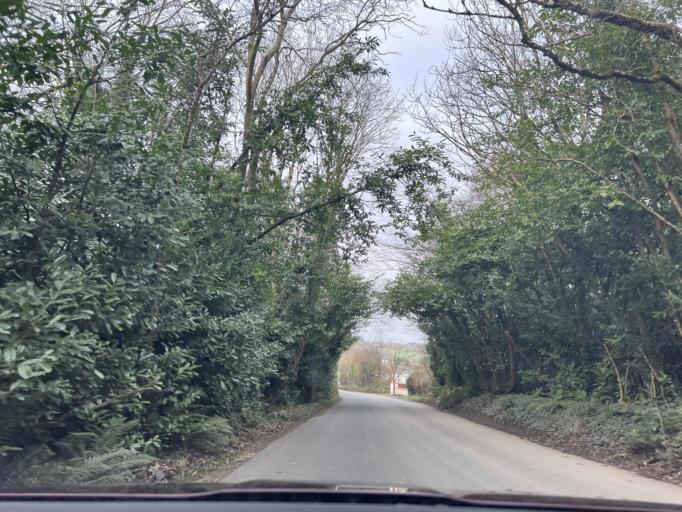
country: IE
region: Leinster
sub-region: Loch Garman
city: Castlebridge
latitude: 52.3818
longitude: -6.5585
